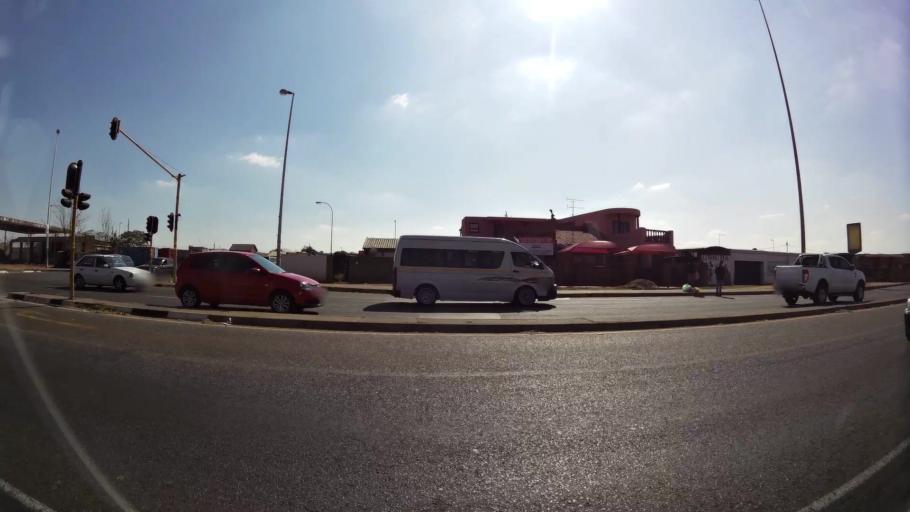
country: ZA
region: Gauteng
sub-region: City of Johannesburg Metropolitan Municipality
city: Soweto
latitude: -26.2782
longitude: 27.8648
